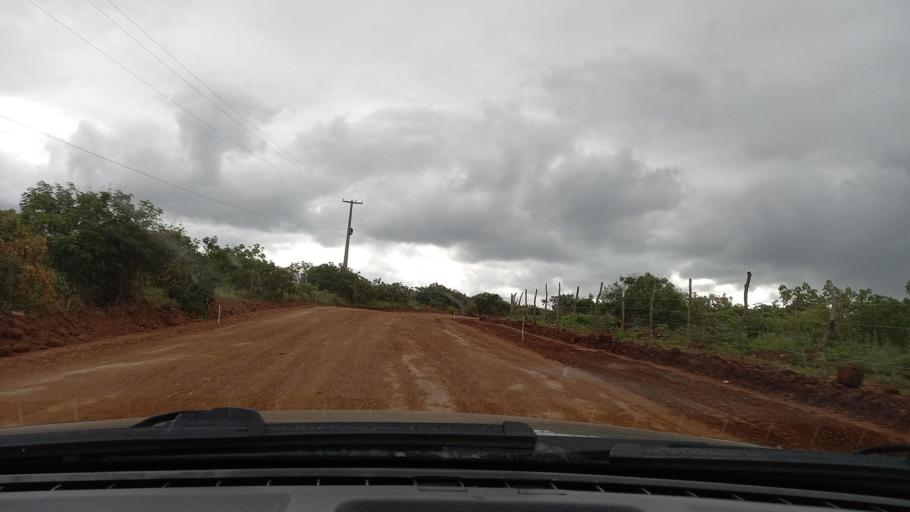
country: BR
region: Sergipe
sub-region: Caninde De Sao Francisco
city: Caninde de Sao Francisco
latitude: -9.6217
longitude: -37.7567
